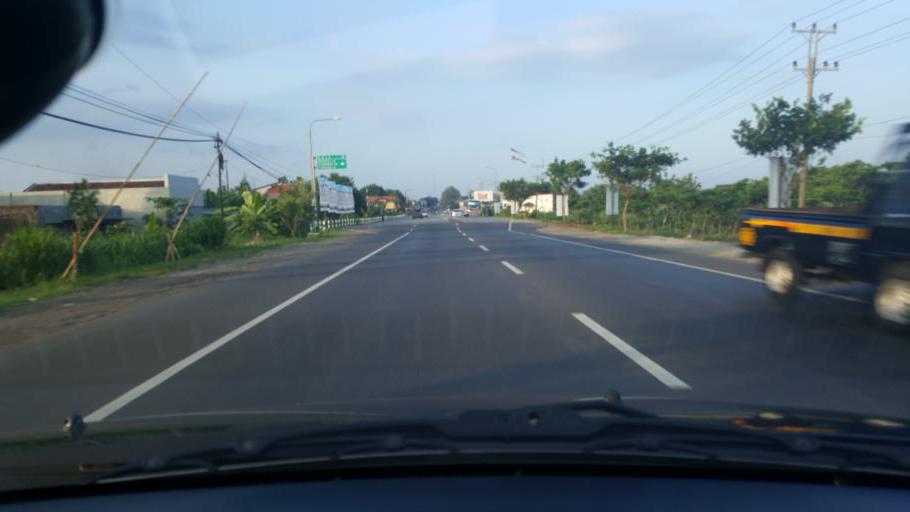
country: ID
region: Central Java
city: Gemiring
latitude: -6.7803
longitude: 110.9904
